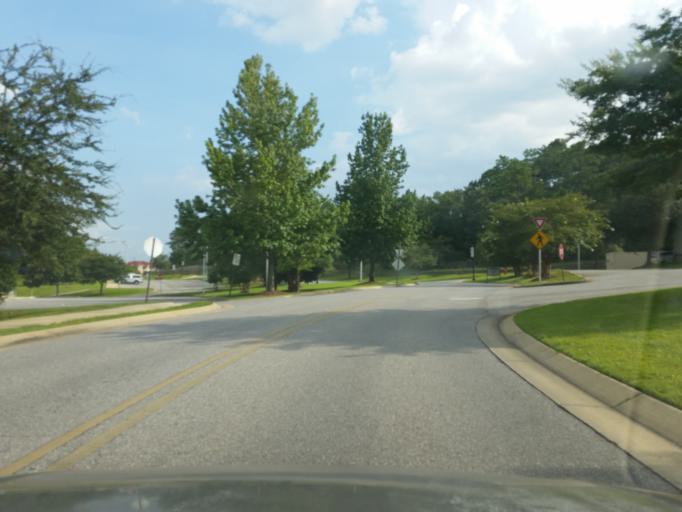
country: US
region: Florida
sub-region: Escambia County
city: Ferry Pass
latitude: 30.5452
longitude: -87.2135
